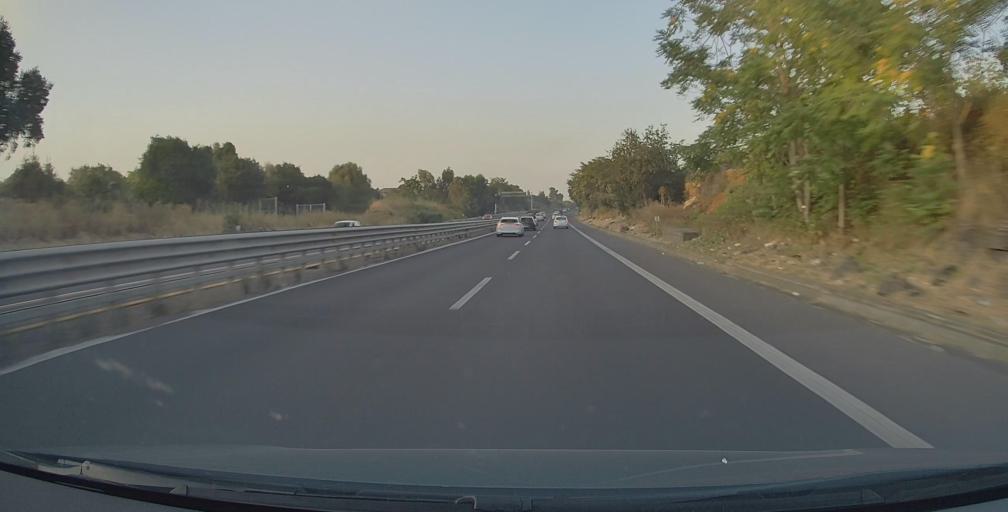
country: IT
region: Sicily
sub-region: Catania
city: San Gregorio di Catania
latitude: 37.5730
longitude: 15.1086
